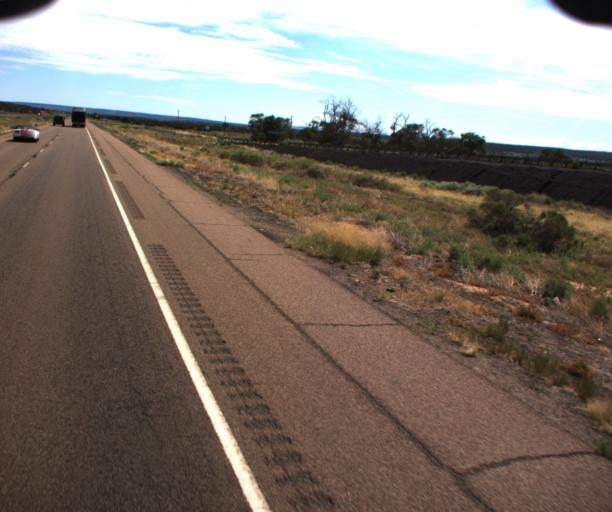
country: US
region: Arizona
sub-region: Apache County
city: Houck
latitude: 35.2385
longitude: -109.3020
